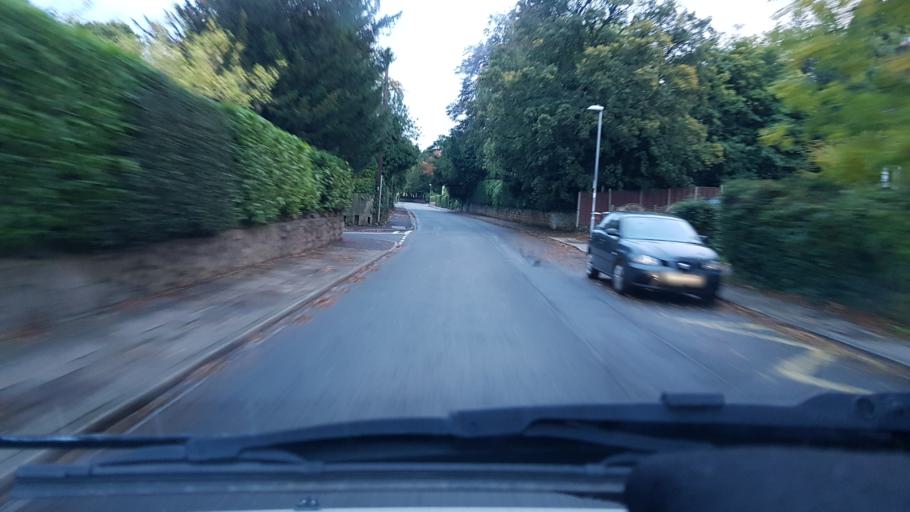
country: GB
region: England
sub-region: Worcestershire
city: Great Malvern
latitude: 52.1152
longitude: -2.3233
